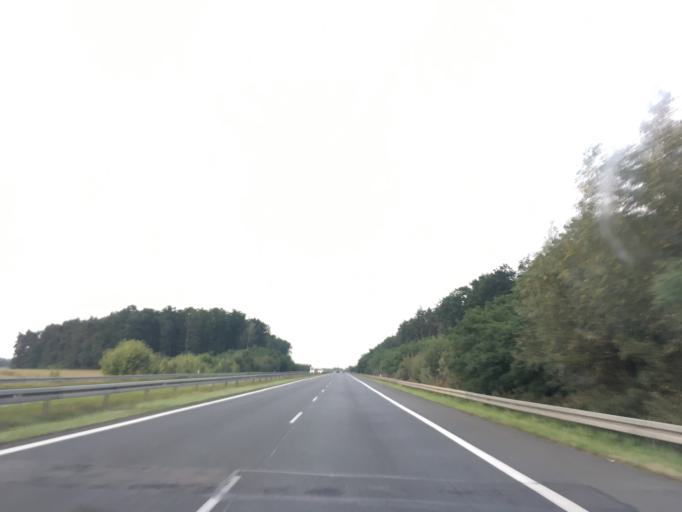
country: PL
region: Lodz Voivodeship
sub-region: Powiat piotrkowski
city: Wola Krzysztoporska
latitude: 51.3053
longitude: 19.5597
